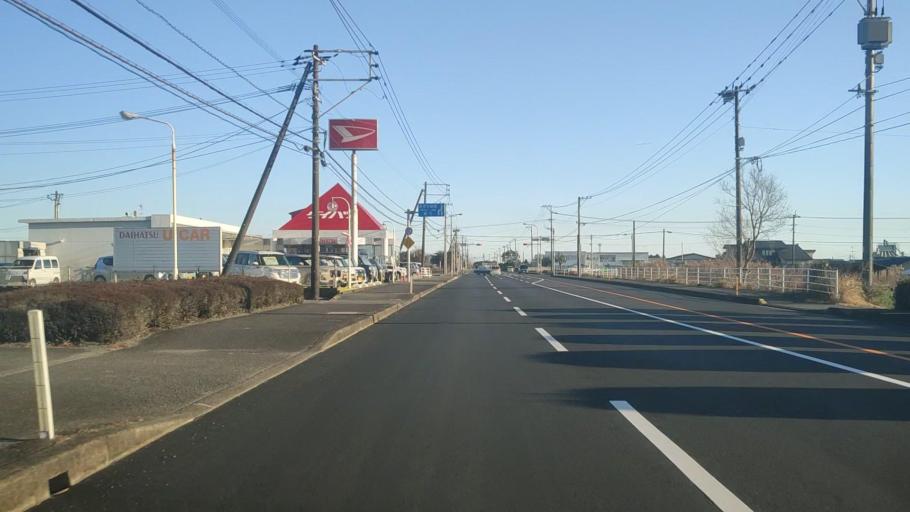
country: JP
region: Miyazaki
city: Takanabe
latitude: 32.2271
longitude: 131.5456
